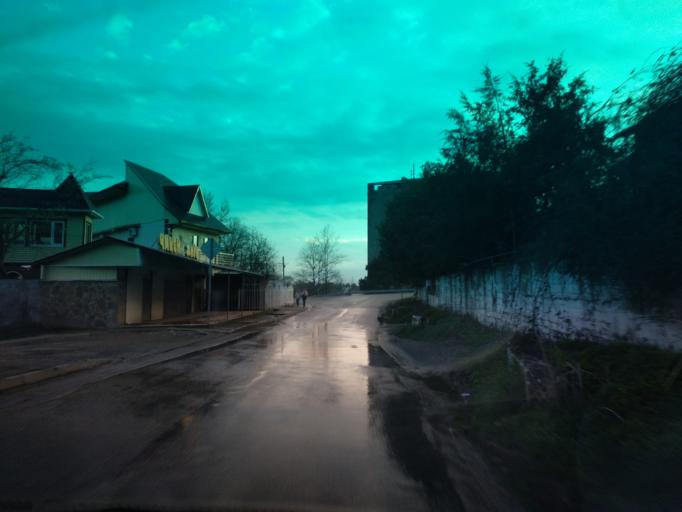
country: RU
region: Krasnodarskiy
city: Novomikhaylovskiy
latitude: 44.2611
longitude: 38.8221
